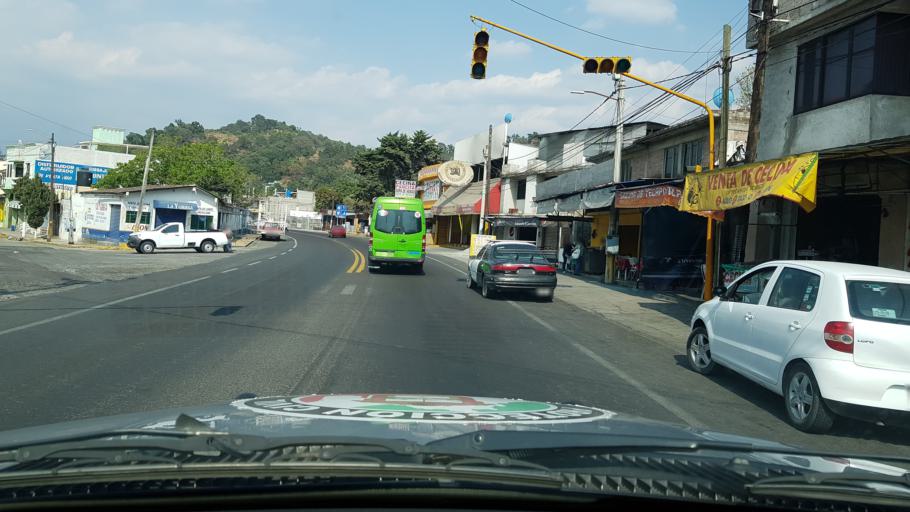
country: MX
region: Mexico
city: Tepetlixpa
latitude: 19.0247
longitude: -98.8190
